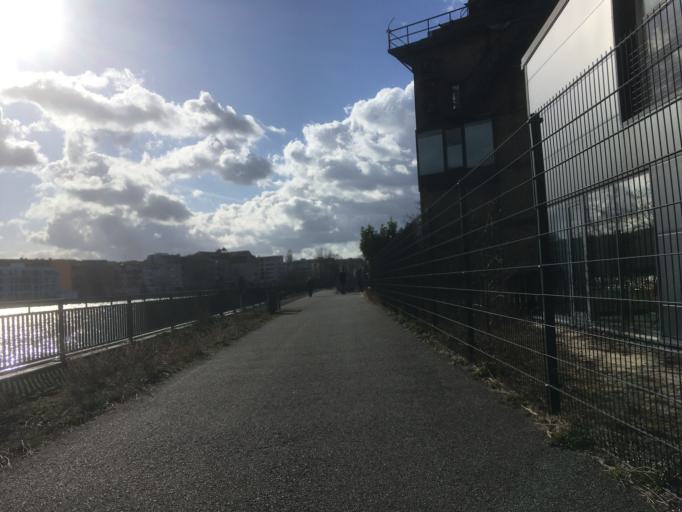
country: DE
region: Berlin
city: Oberschoneweide
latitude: 52.4542
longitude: 13.5294
